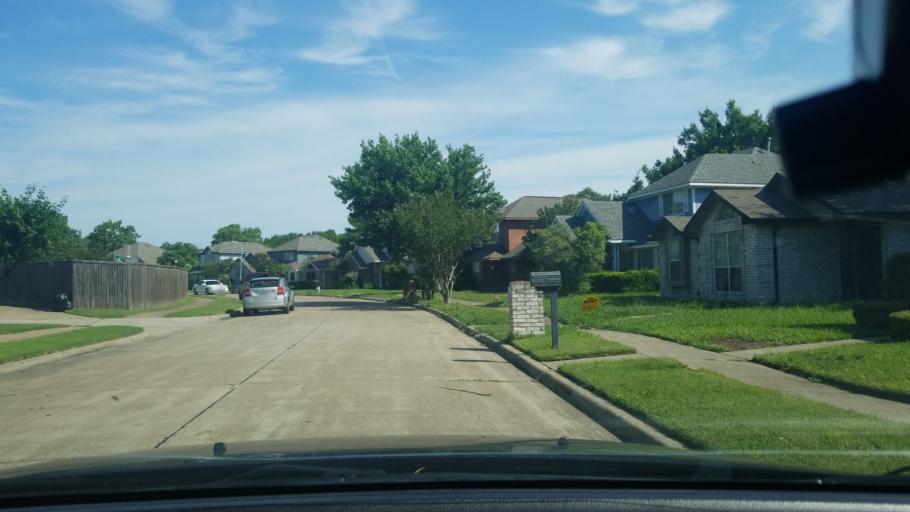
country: US
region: Texas
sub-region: Dallas County
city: Mesquite
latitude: 32.7730
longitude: -96.5762
